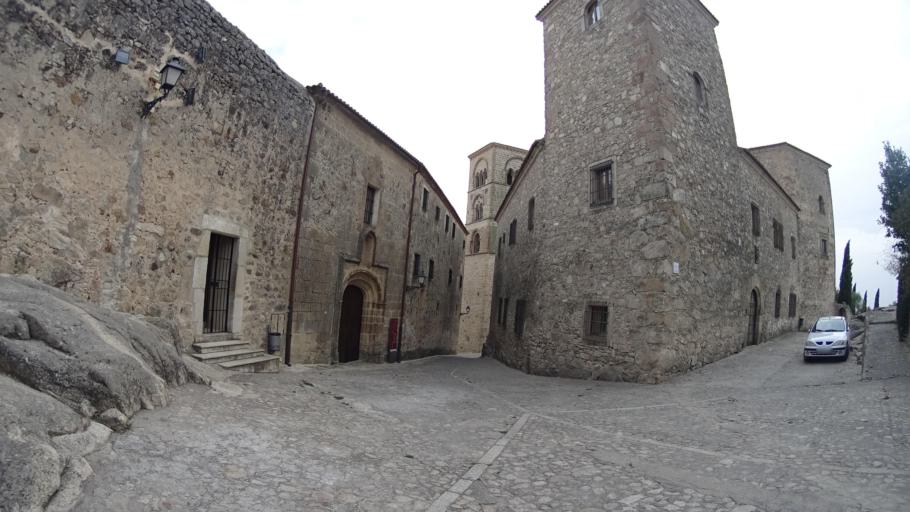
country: ES
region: Extremadura
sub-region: Provincia de Caceres
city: Trujillo
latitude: 39.4614
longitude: -5.8841
